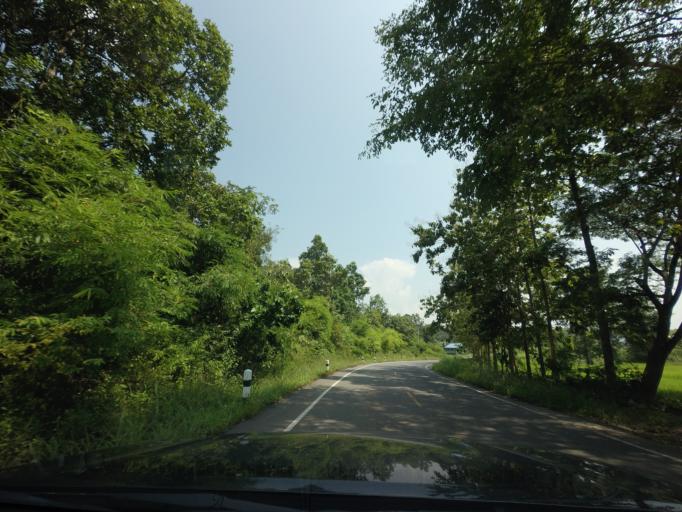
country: TH
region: Nan
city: Nan
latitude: 18.8555
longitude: 100.7996
